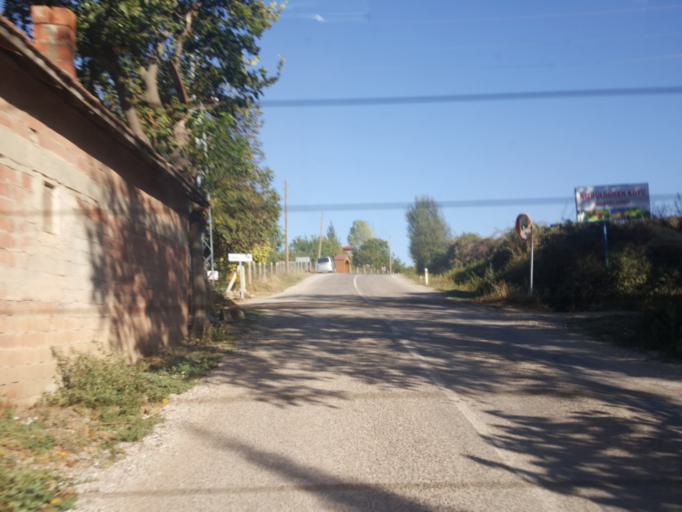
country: TR
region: Amasya
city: Tasova
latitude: 40.7144
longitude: 36.3228
